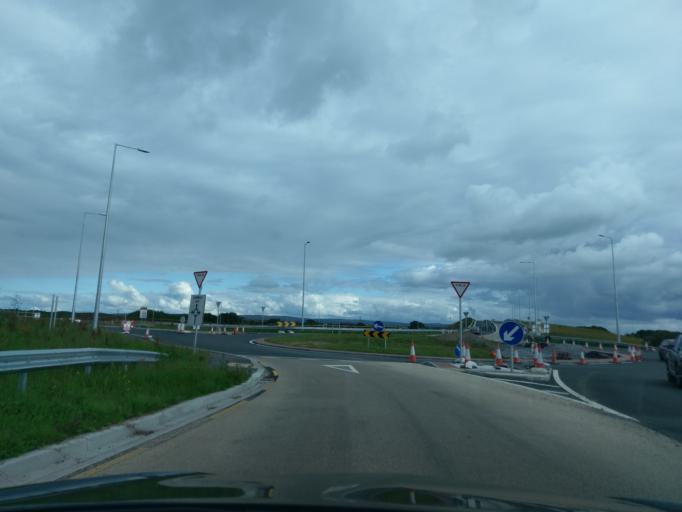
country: IE
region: Connaught
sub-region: County Galway
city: Gort
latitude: 53.1789
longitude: -8.8397
